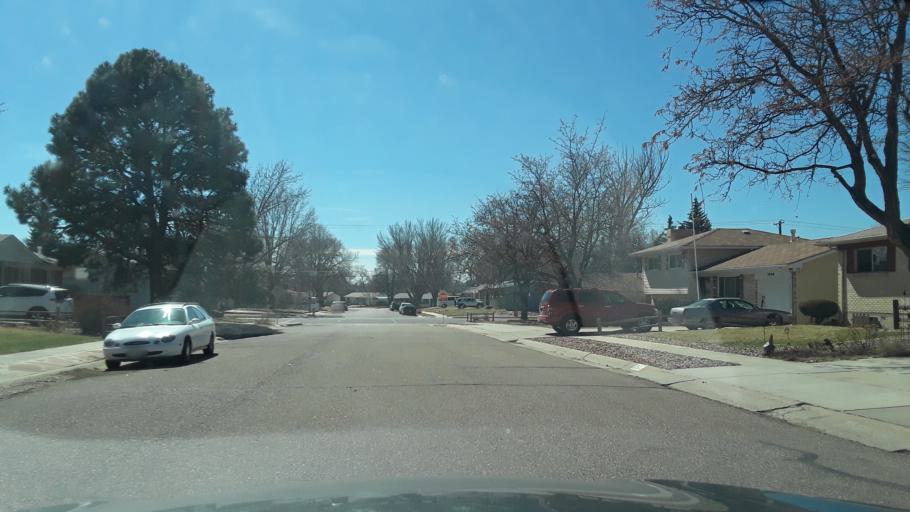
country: US
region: Colorado
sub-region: El Paso County
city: Colorado Springs
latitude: 38.8728
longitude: -104.8089
